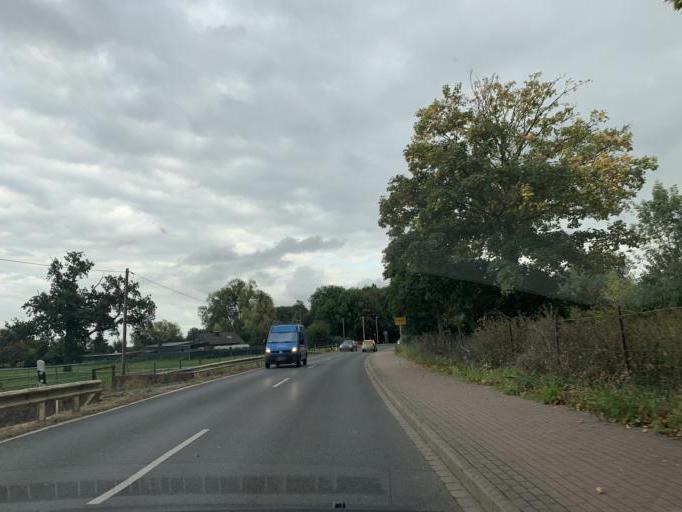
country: DE
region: North Rhine-Westphalia
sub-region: Regierungsbezirk Koln
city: Linnich
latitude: 51.0008
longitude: 6.2519
